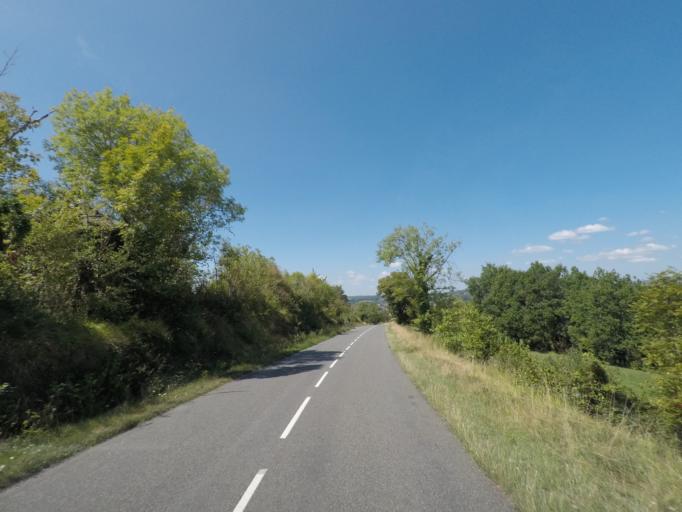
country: FR
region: Midi-Pyrenees
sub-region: Departement du Lot
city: Figeac
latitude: 44.6048
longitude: 2.0619
